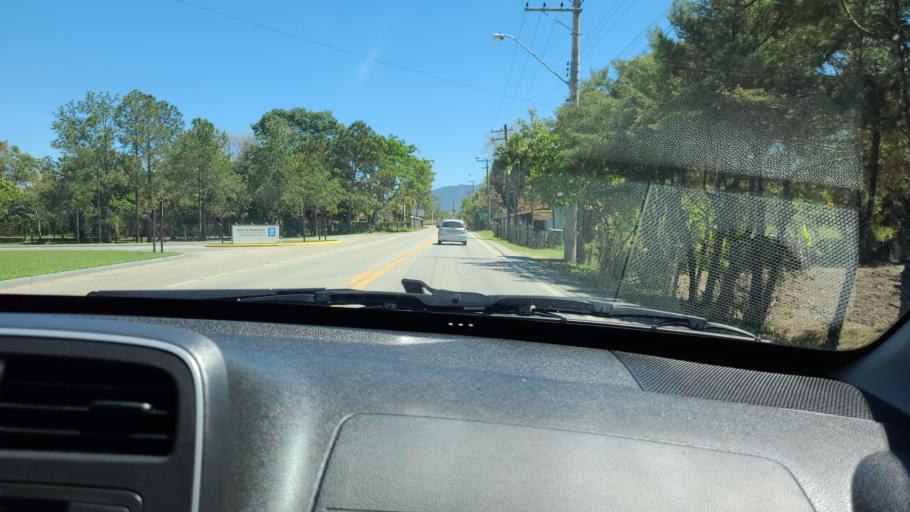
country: BR
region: Sao Paulo
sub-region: Tremembe
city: Tremembe
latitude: -22.8863
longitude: -45.5378
